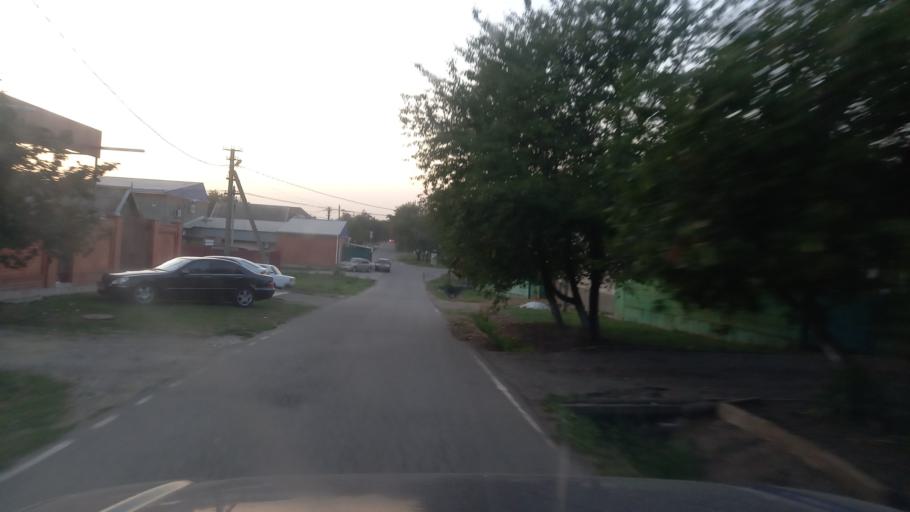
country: RU
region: Adygeya
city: Enem
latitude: 44.9324
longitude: 38.9080
